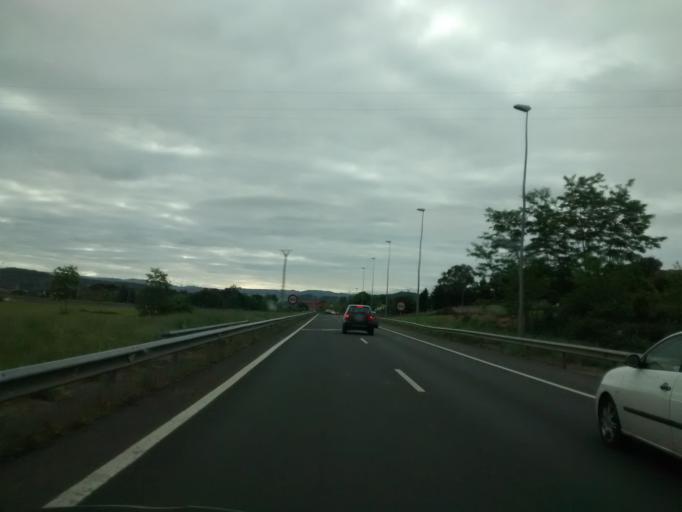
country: ES
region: Cantabria
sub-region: Provincia de Cantabria
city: Torrelavega
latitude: 43.3494
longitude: -4.0311
